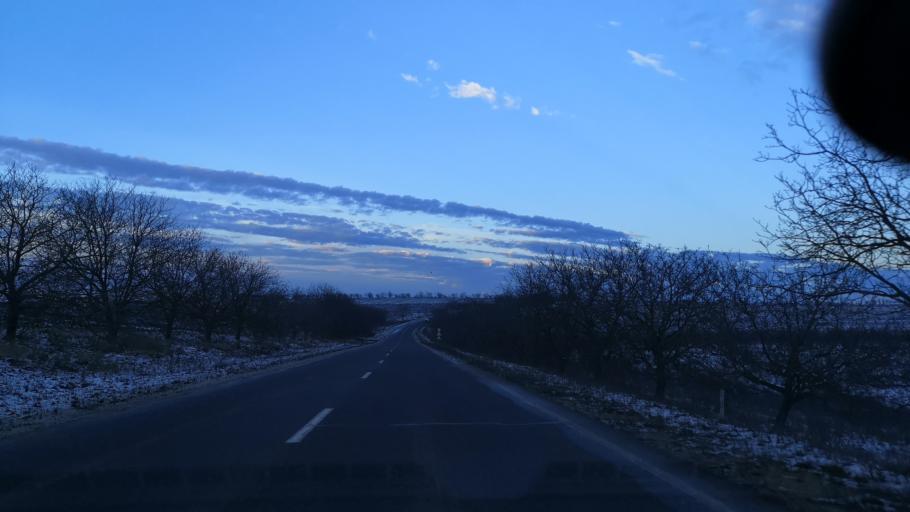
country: MD
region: Orhei
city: Orhei
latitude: 47.5696
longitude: 28.7973
